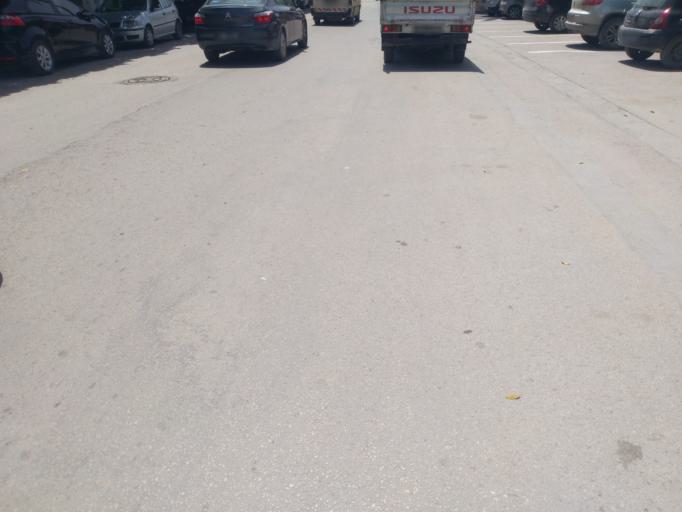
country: TN
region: Al Qayrawan
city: Kairouan
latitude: 35.6734
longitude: 10.1027
